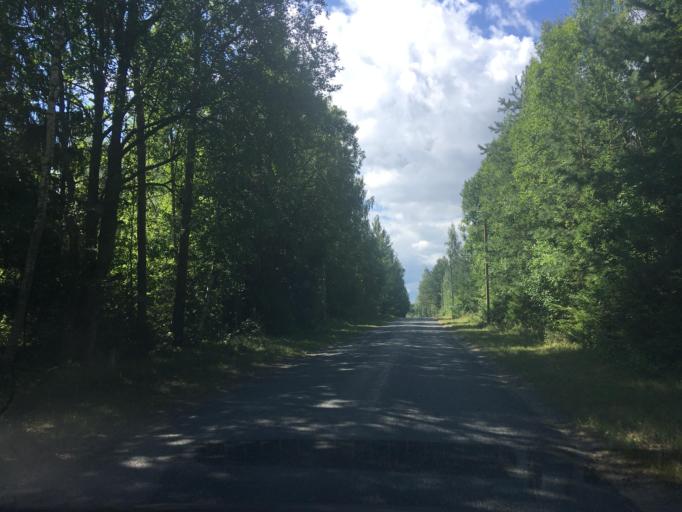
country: EE
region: Tartu
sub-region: Puhja vald
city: Puhja
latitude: 58.2419
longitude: 26.1759
